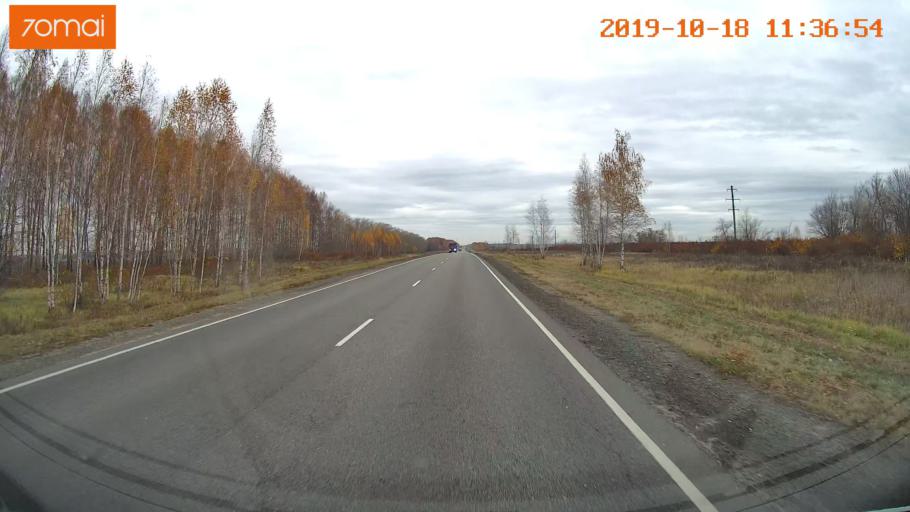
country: RU
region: Rjazan
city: Oktyabr'skiy
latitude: 54.1457
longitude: 38.8174
